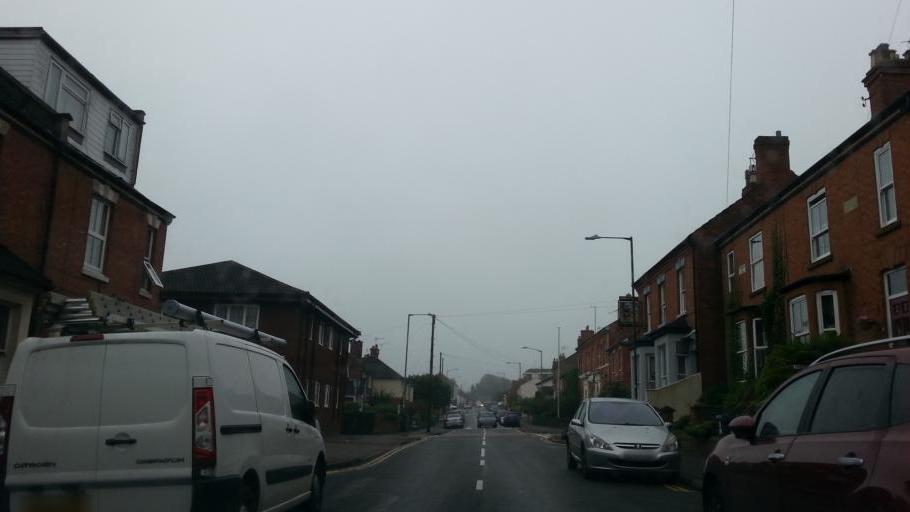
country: GB
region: England
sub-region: Warwickshire
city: Kenilworth
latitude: 52.3506
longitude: -1.5712
